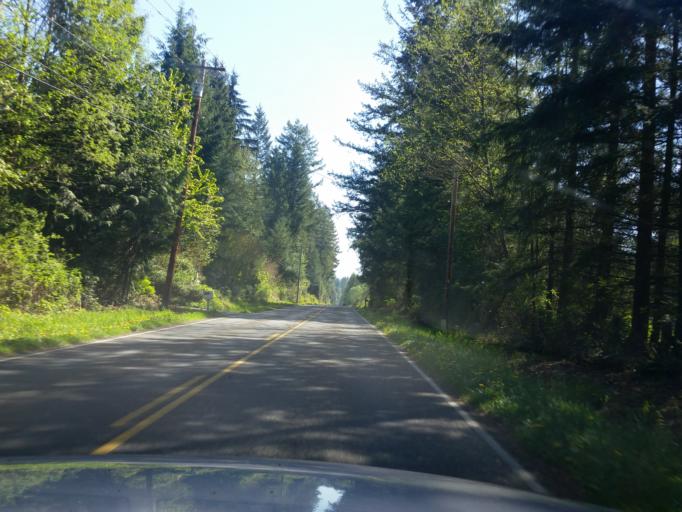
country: US
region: Washington
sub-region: Snohomish County
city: Machias
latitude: 47.9634
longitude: -122.0364
